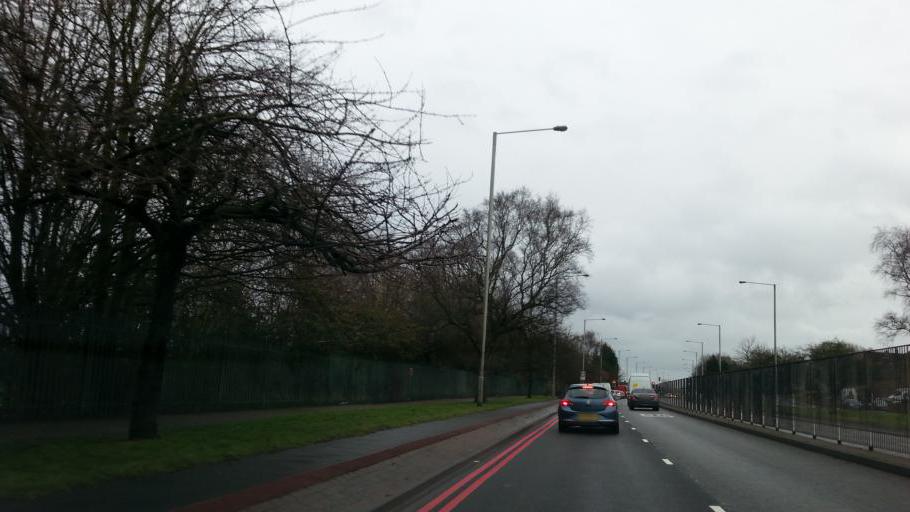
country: GB
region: England
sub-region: Sandwell
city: Rowley Regis
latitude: 52.5090
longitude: -2.0420
